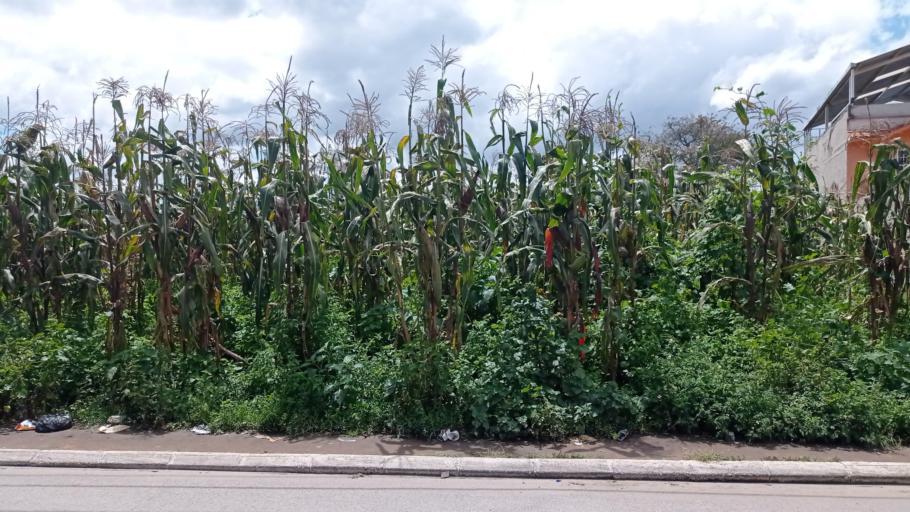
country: GT
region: Quetzaltenango
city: Olintepeque
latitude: 14.8677
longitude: -91.5068
